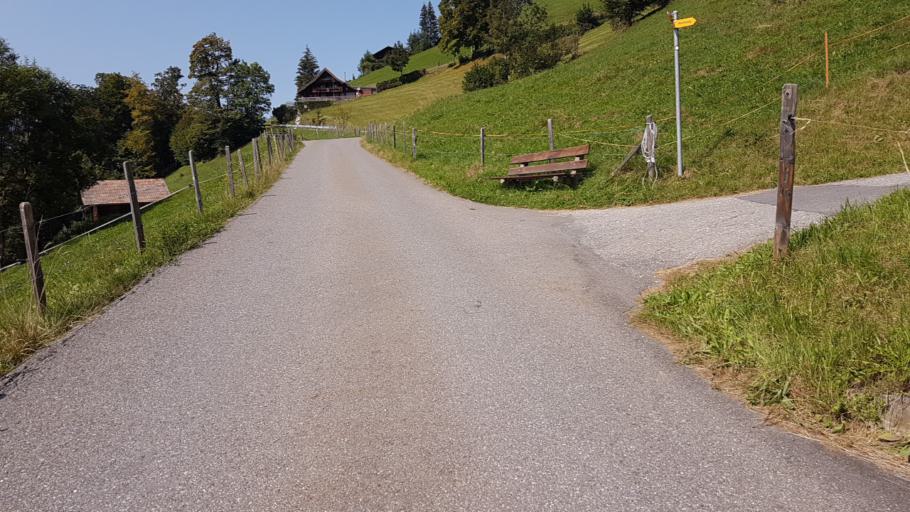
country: CH
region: Bern
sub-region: Frutigen-Niedersimmental District
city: Aeschi
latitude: 46.5929
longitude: 7.7179
